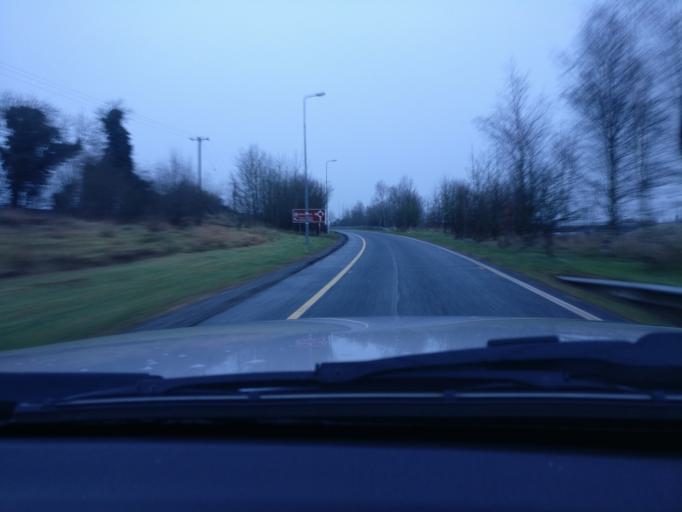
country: IE
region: Leinster
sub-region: An Iarmhi
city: Rochfortbridge
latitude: 53.3870
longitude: -7.3649
